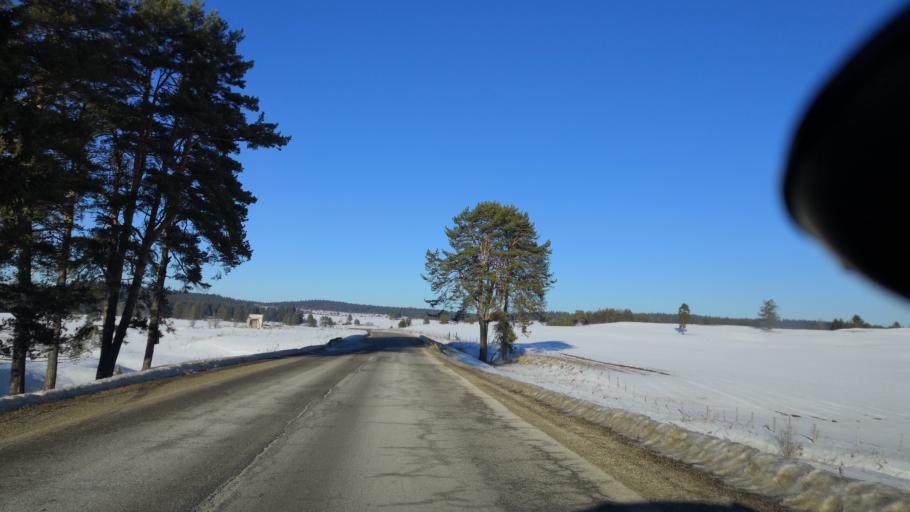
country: BA
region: Republika Srpska
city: Han Pijesak
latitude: 44.0310
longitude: 18.9048
